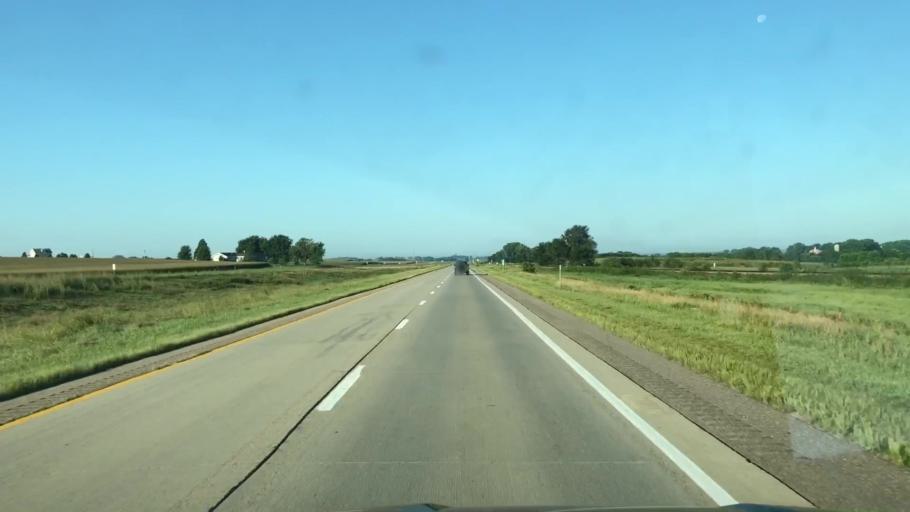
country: US
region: Iowa
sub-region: Sioux County
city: Alton
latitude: 43.0291
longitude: -95.9360
